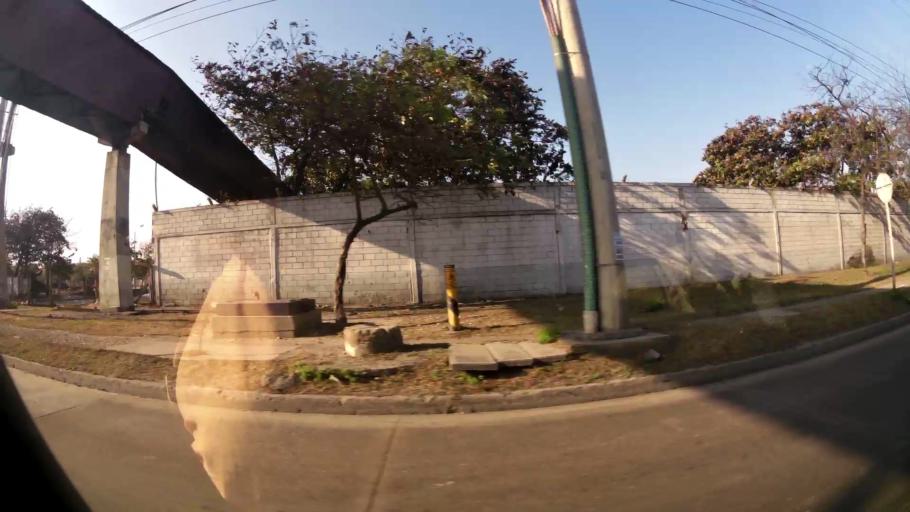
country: CO
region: Atlantico
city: Barranquilla
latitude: 11.0363
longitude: -74.8157
